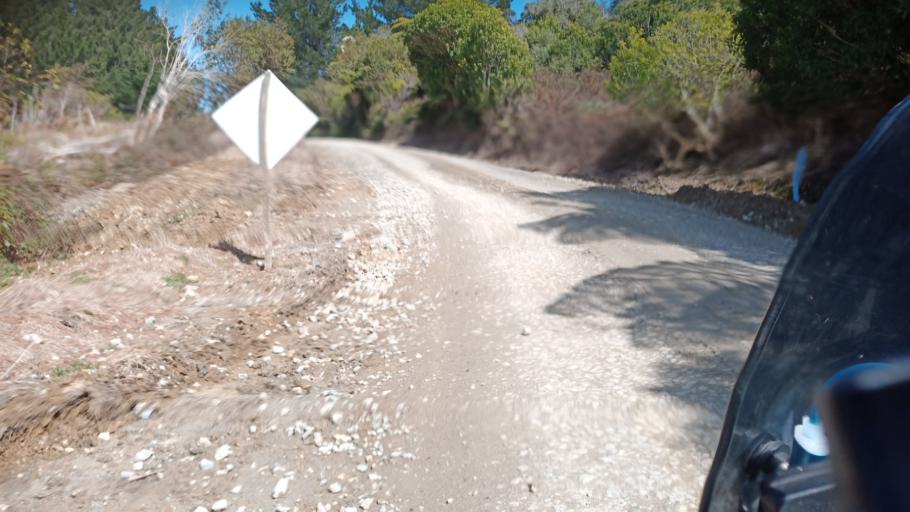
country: NZ
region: Gisborne
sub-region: Gisborne District
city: Gisborne
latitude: -38.8707
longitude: 177.7888
